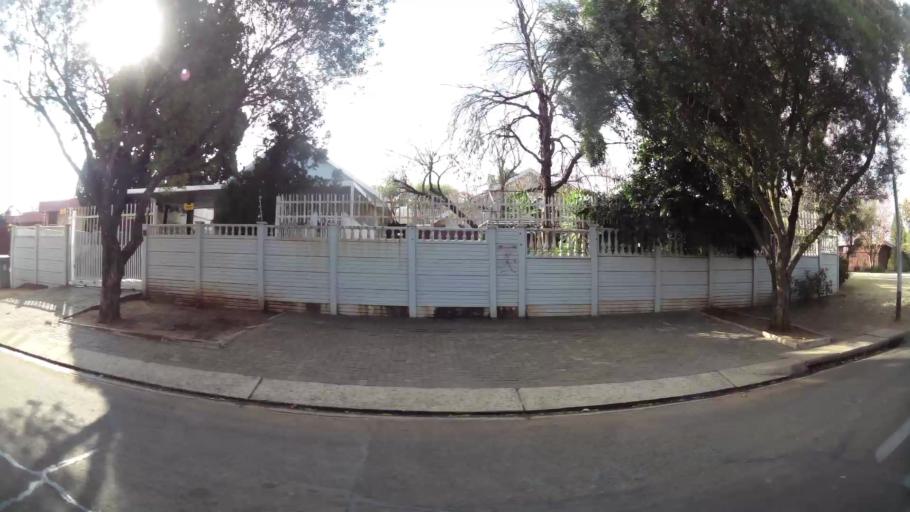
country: ZA
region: Orange Free State
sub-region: Mangaung Metropolitan Municipality
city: Bloemfontein
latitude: -29.0787
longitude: 26.2298
